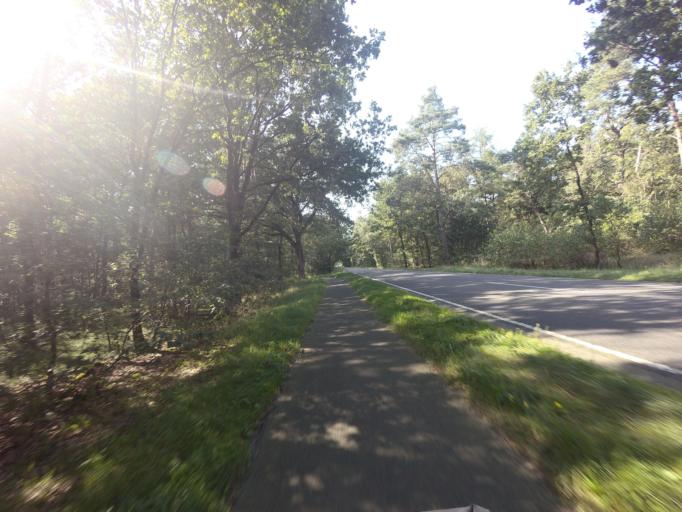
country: DE
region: Lower Saxony
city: Wielen
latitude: 52.5294
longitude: 6.7216
